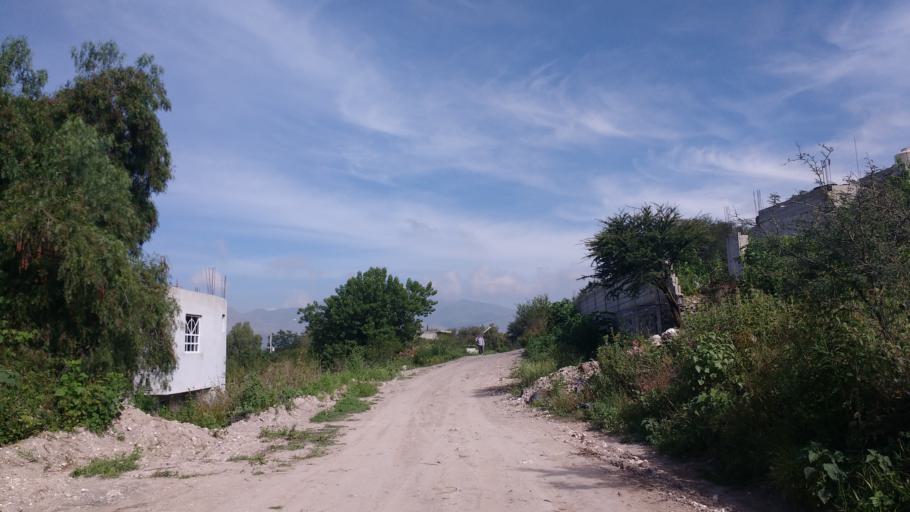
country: MX
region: Hidalgo
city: Mixquiahuala de Juarez
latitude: 20.2505
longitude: -99.2415
